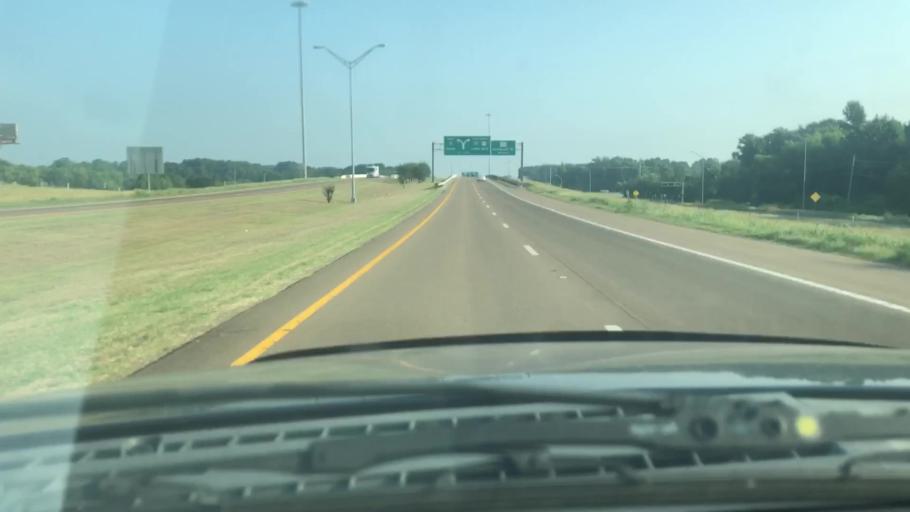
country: US
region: Texas
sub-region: Bowie County
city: Wake Village
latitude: 33.4278
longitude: -94.0959
